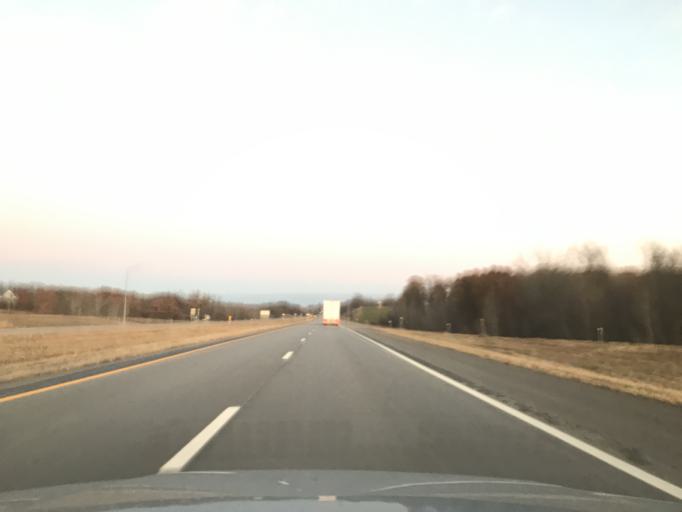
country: US
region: Missouri
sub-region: Marion County
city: Hannibal
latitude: 39.7141
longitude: -91.4166
